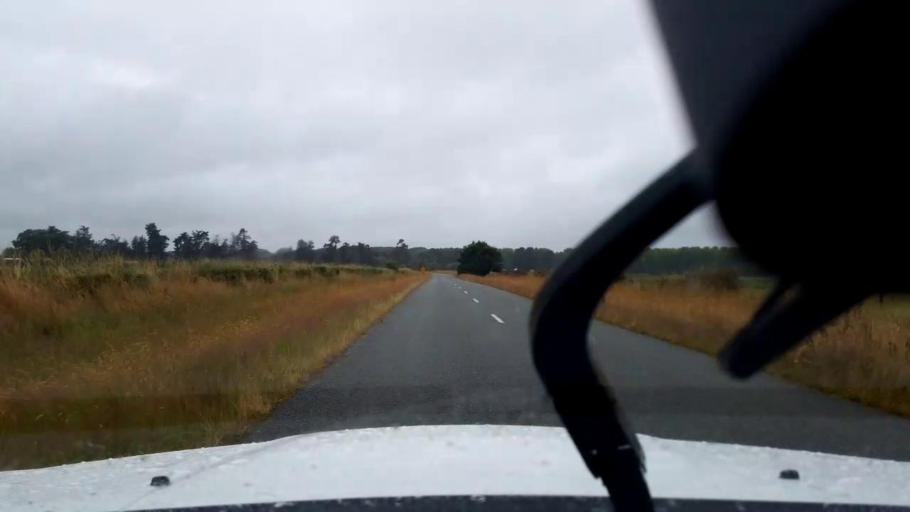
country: NZ
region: Canterbury
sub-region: Timaru District
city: Pleasant Point
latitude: -44.2526
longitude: 171.2374
